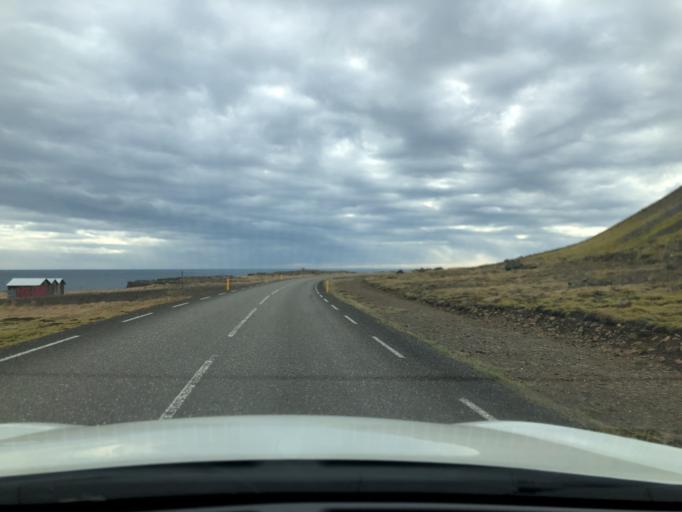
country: IS
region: East
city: Neskaupstadur
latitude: 64.8724
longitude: -13.7739
